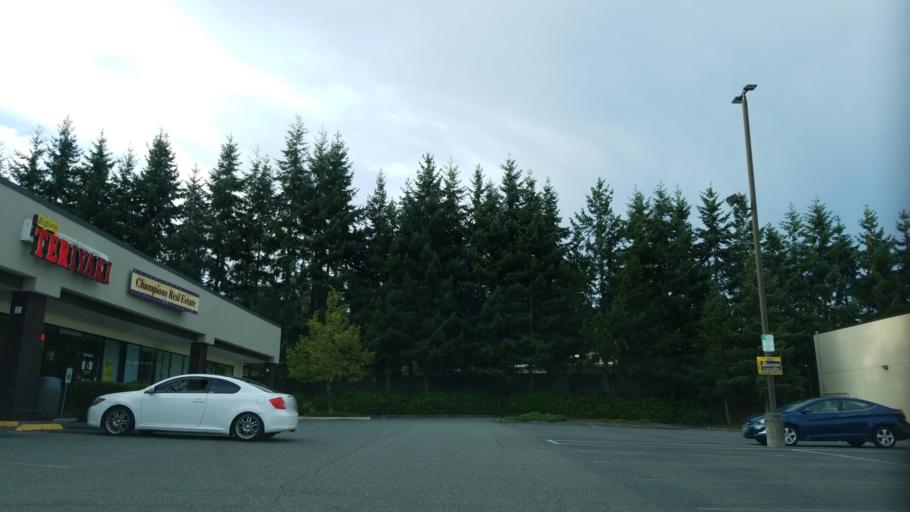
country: US
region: Washington
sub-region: Snohomish County
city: Lynnwood
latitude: 47.8233
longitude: -122.3162
